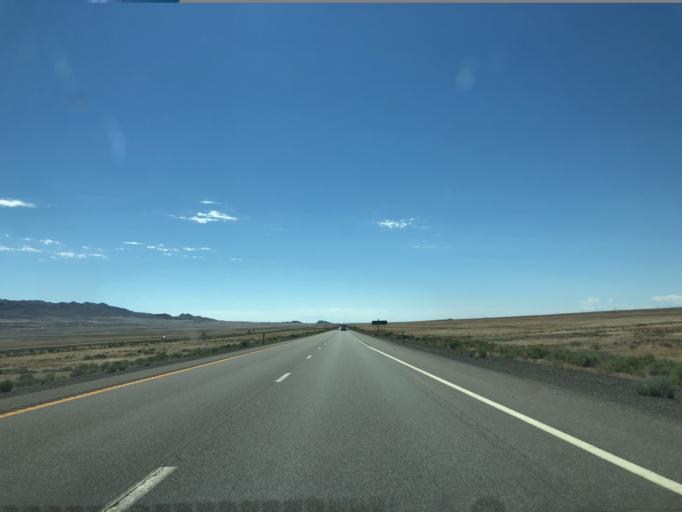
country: US
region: Nevada
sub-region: Elko County
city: West Wendover
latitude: 40.8372
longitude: -114.2045
